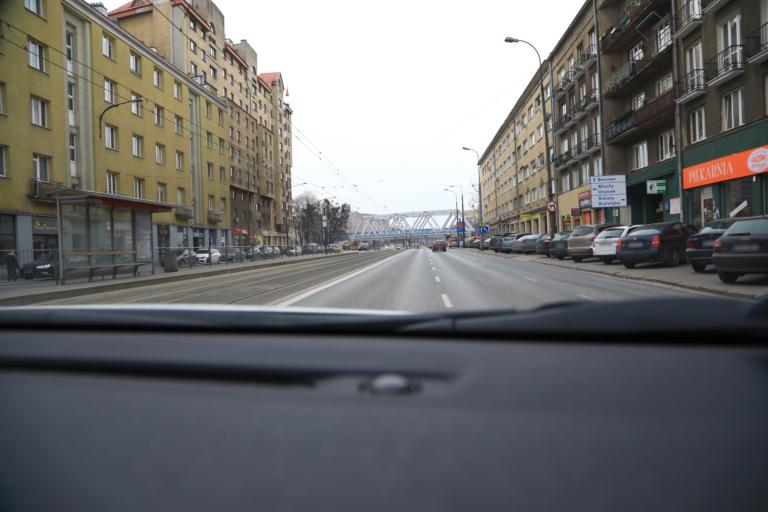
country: PL
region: Masovian Voivodeship
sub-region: Warszawa
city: Ochota
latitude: 52.2324
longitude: 20.9605
